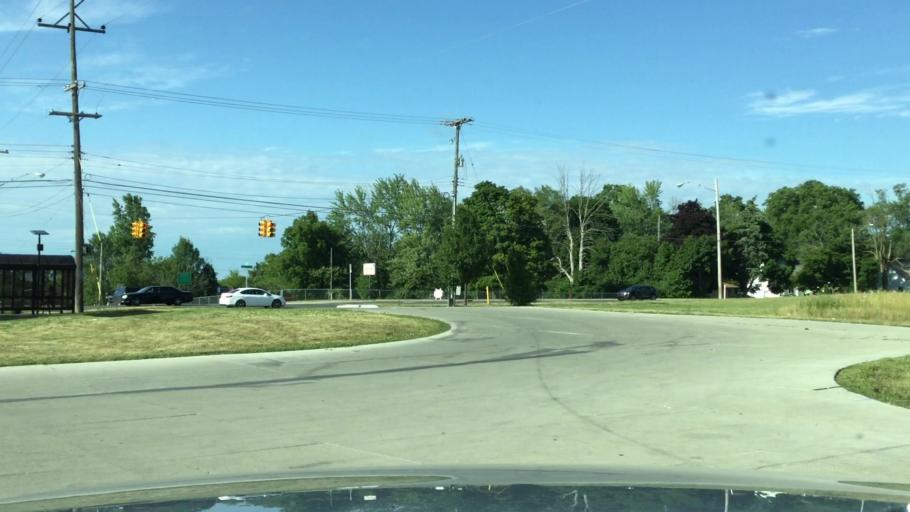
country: US
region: Michigan
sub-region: Genesee County
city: Beecher
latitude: 43.0896
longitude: -83.7144
